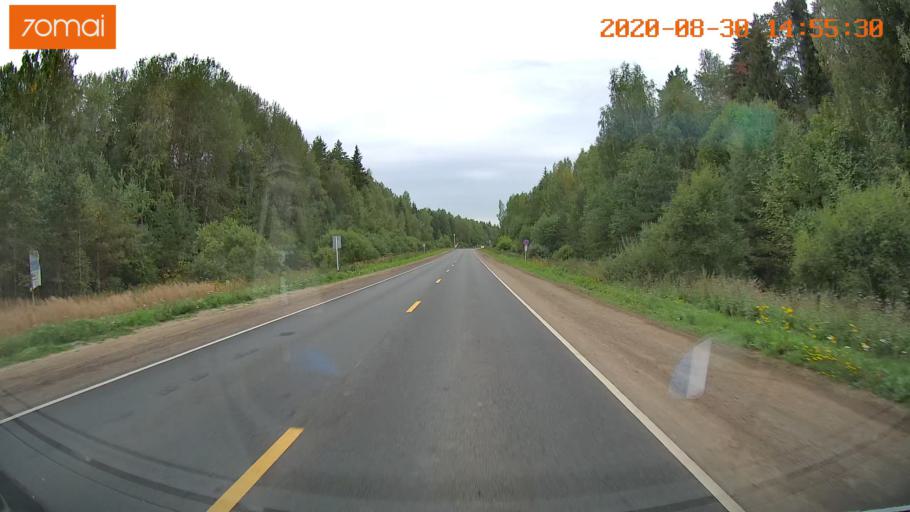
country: RU
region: Ivanovo
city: Kineshma
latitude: 57.3835
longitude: 42.0353
